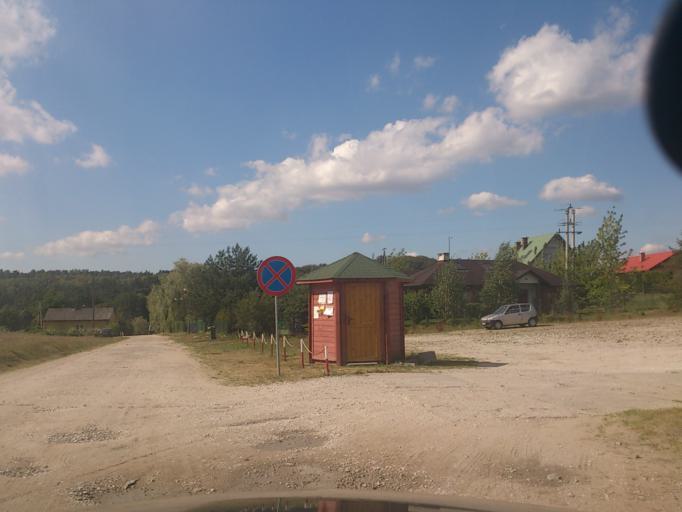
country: PL
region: Kujawsko-Pomorskie
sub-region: Powiat golubsko-dobrzynski
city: Golub-Dobrzyn
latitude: 53.0748
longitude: 19.0307
